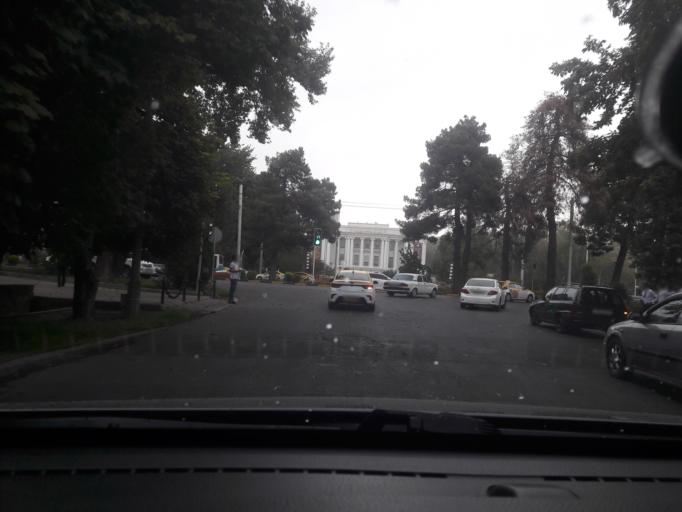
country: TJ
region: Dushanbe
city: Dushanbe
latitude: 38.5673
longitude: 68.7928
